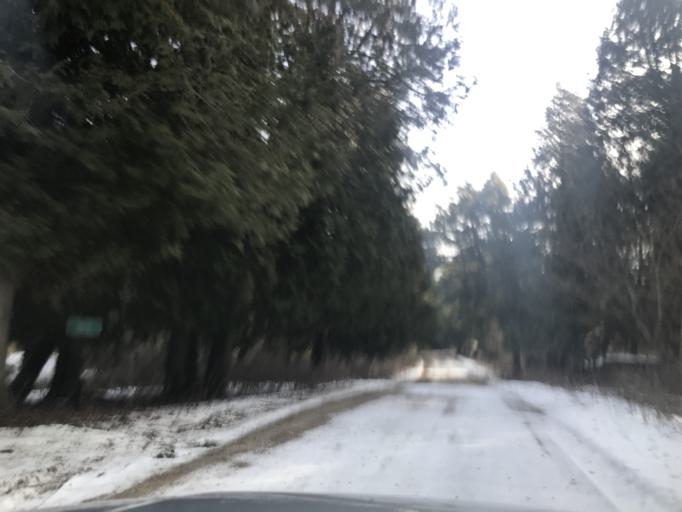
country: US
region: Wisconsin
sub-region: Door County
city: Sturgeon Bay
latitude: 45.1484
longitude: -87.0333
